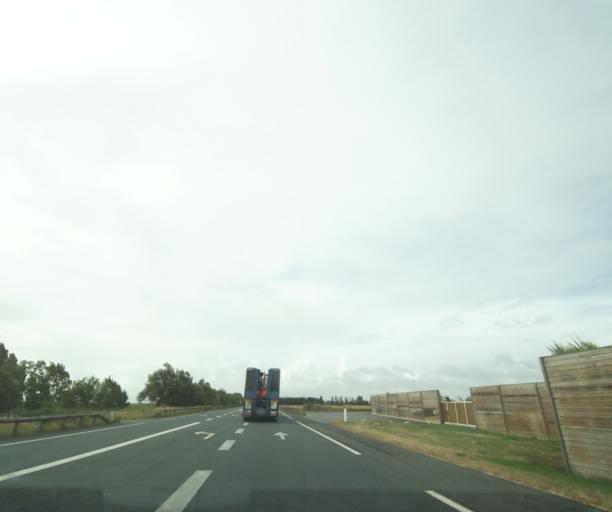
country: FR
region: Pays de la Loire
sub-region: Departement de la Vendee
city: Champagne-les-Marais
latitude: 46.4093
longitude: -1.0985
